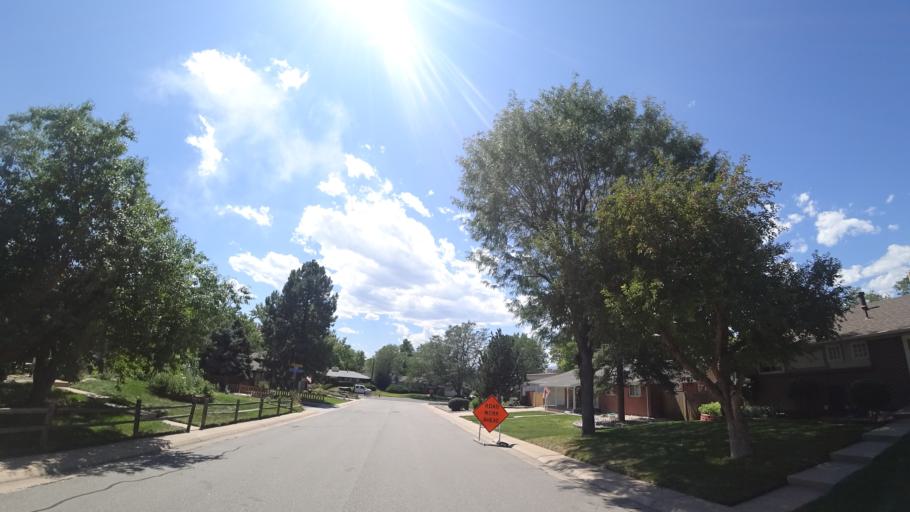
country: US
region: Colorado
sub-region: Arapahoe County
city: Greenwood Village
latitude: 39.6077
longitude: -104.9833
